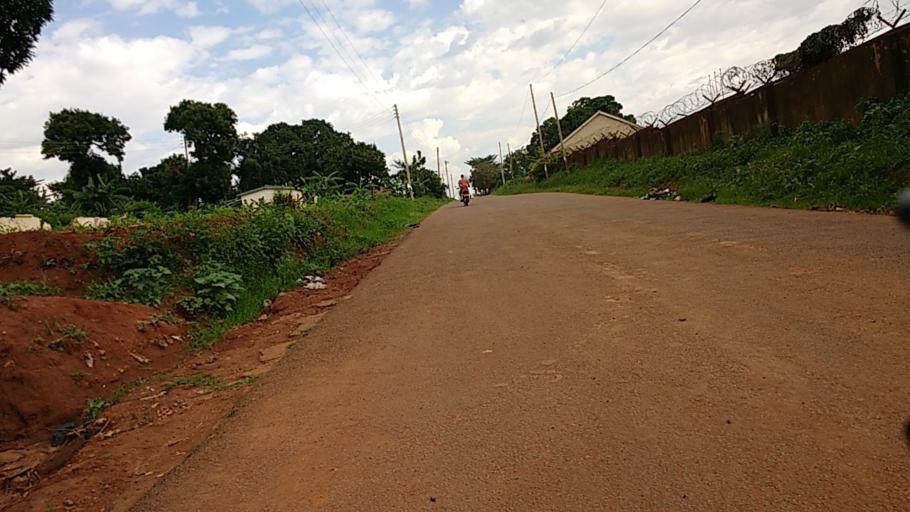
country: UG
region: Eastern Region
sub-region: Mbale District
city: Mbale
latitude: 1.0715
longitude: 34.1694
